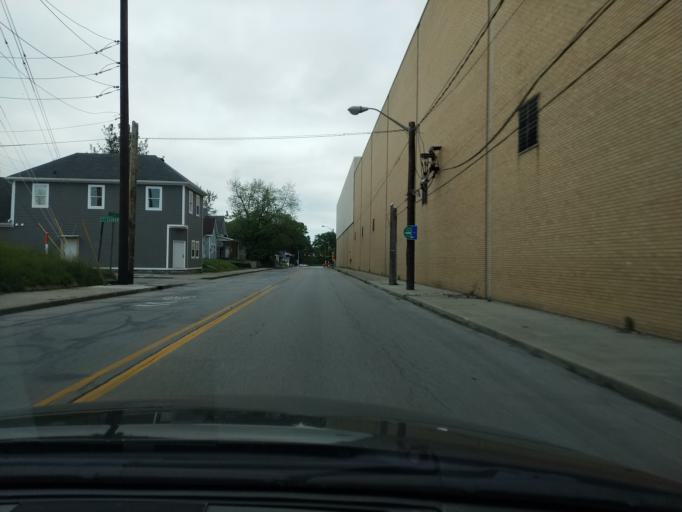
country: US
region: Indiana
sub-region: Marion County
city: Indianapolis
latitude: 39.7397
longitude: -86.1495
